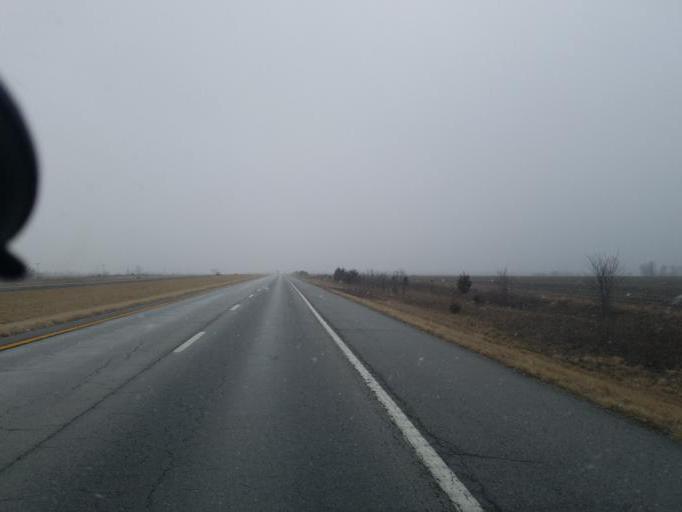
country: US
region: Missouri
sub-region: Macon County
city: La Plata
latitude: 39.9469
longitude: -92.4771
